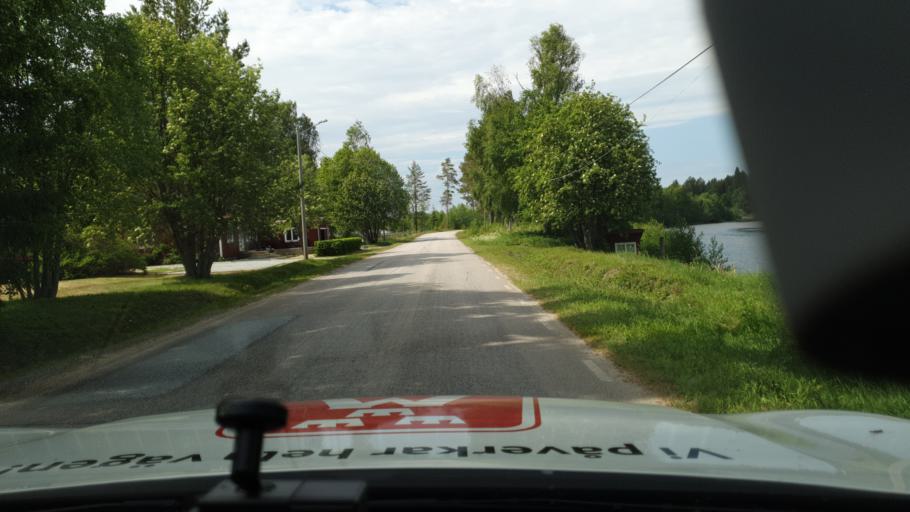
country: SE
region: Vaesterbotten
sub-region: Umea Kommun
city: Hoernefors
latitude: 63.5399
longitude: 19.7144
